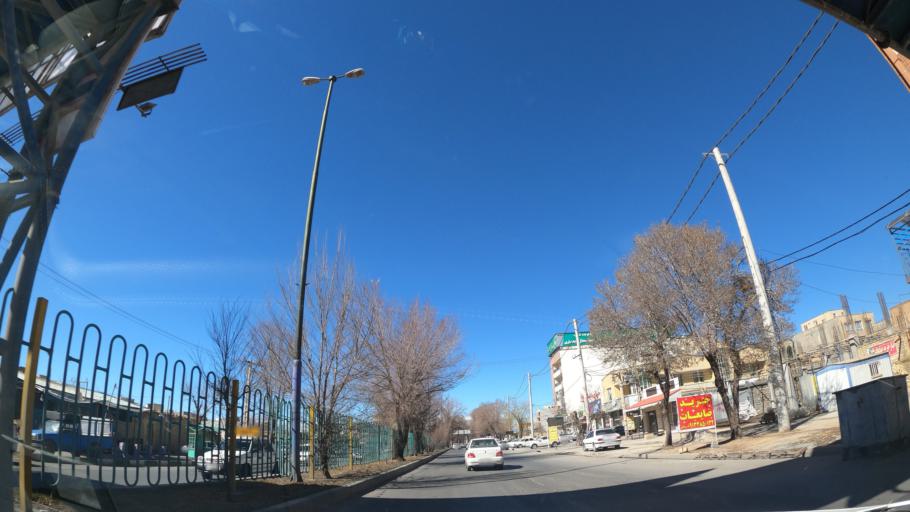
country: IR
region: Chahar Mahall va Bakhtiari
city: Shahrekord
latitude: 32.3108
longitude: 50.8882
